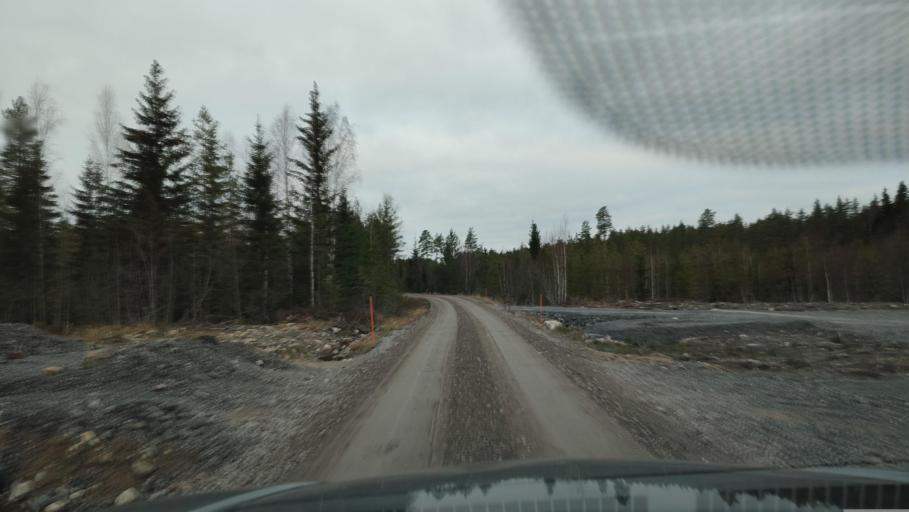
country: FI
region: Southern Ostrobothnia
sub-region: Suupohja
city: Karijoki
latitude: 62.2044
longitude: 21.5847
